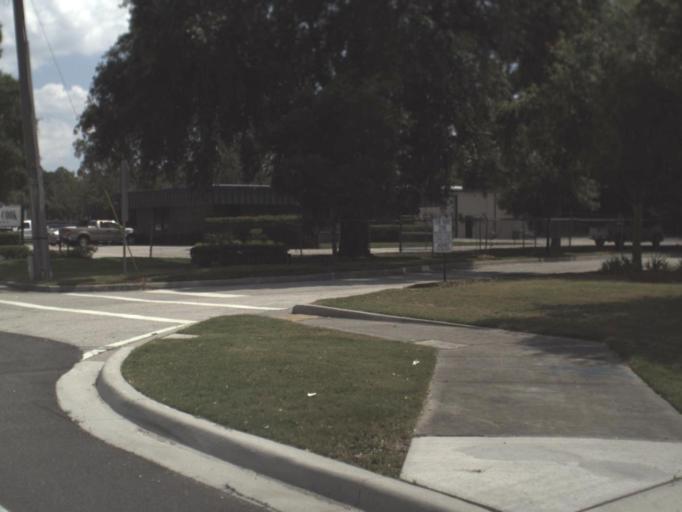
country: US
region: Florida
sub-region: Saint Johns County
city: Fruit Cove
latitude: 30.2060
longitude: -81.5769
